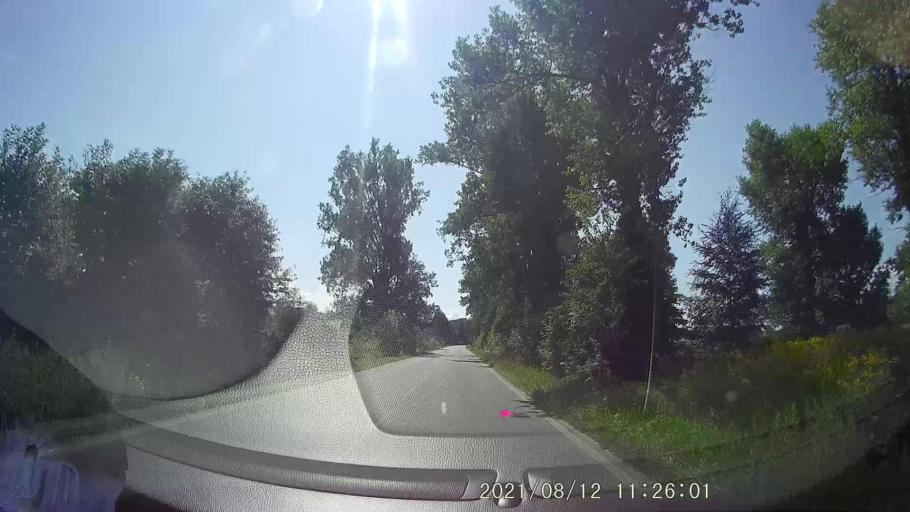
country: PL
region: Lower Silesian Voivodeship
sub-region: Powiat klodzki
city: Bystrzyca Klodzka
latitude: 50.2808
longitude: 16.6829
